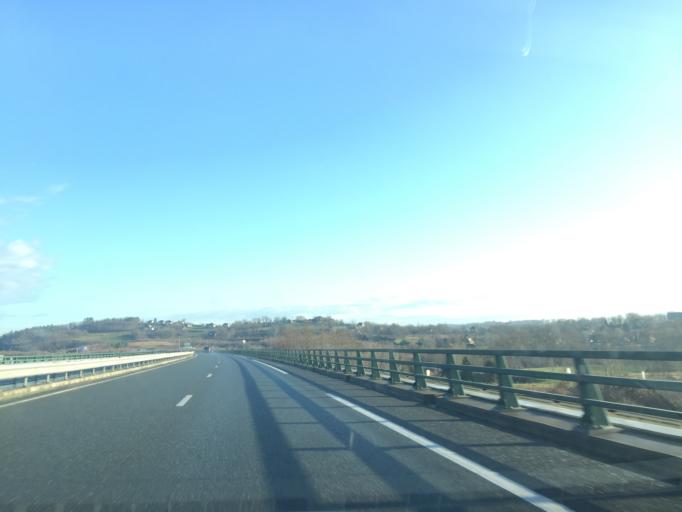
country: FR
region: Limousin
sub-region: Departement de la Correze
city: Varetz
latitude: 45.1668
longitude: 1.4621
